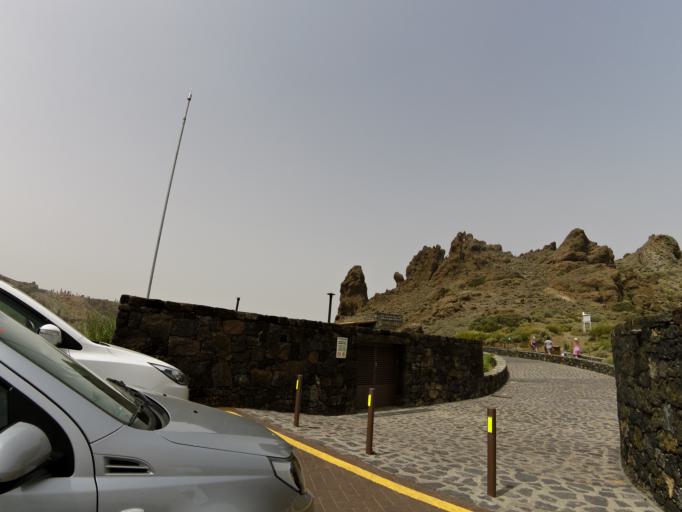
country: ES
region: Canary Islands
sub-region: Provincia de Santa Cruz de Tenerife
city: Vilaflor
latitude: 28.2127
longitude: -16.6812
